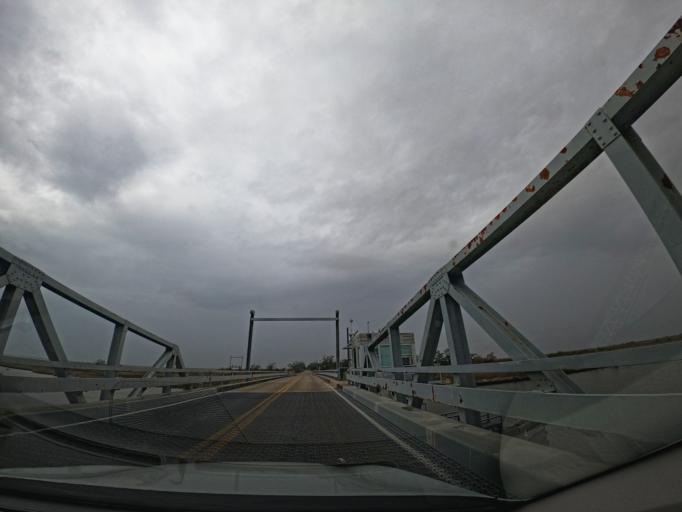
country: US
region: Louisiana
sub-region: Cameron Parish
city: Cameron
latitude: 29.7704
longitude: -93.0134
